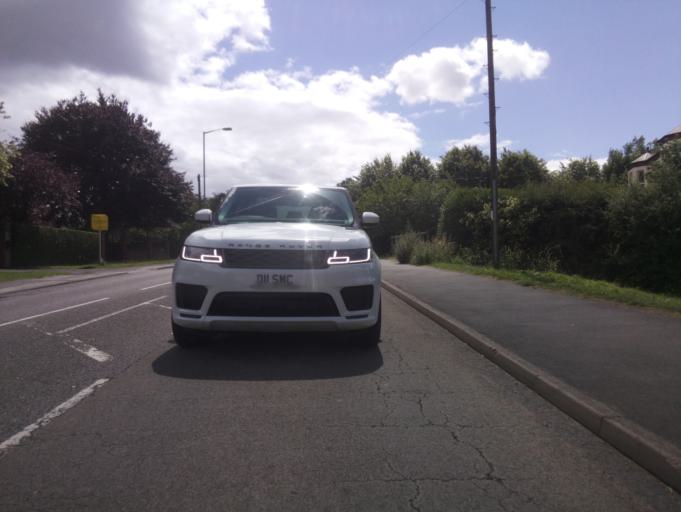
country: GB
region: England
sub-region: Nottinghamshire
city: Arnold
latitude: 52.9969
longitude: -1.1031
